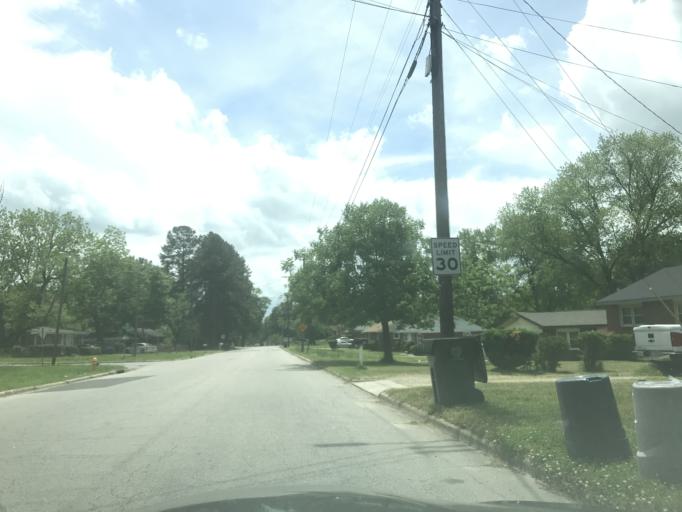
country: US
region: North Carolina
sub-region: Wake County
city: Raleigh
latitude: 35.7708
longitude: -78.5946
